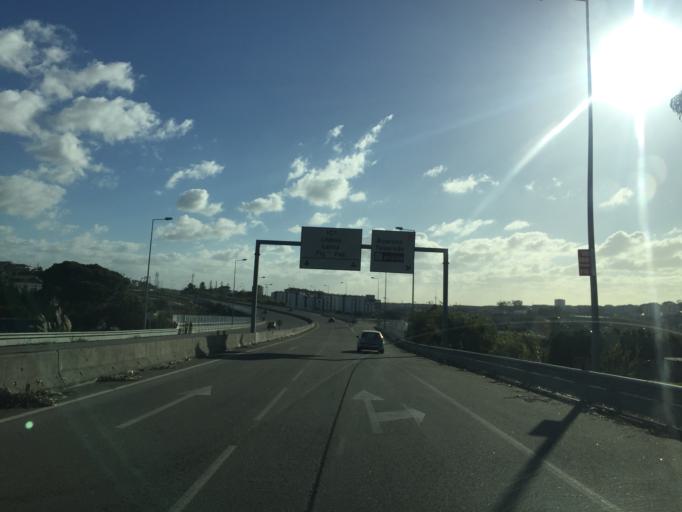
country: PT
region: Coimbra
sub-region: Figueira da Foz
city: Tavarede
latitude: 40.1670
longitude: -8.8393
